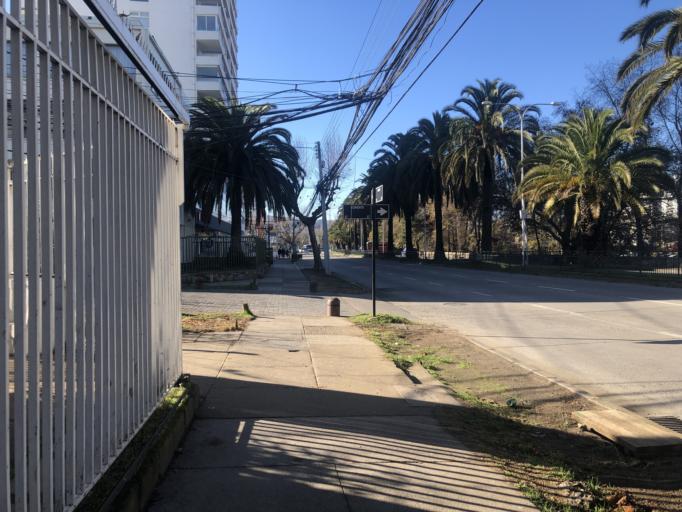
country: CL
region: Valparaiso
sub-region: Provincia de Valparaiso
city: Vina del Mar
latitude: -33.0226
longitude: -71.5504
